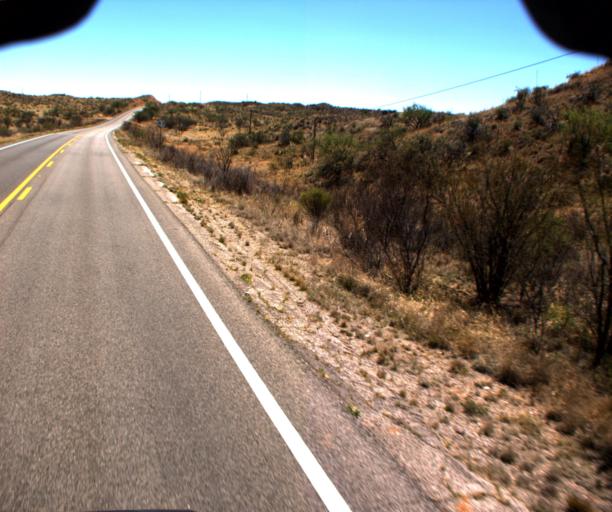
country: US
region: Arizona
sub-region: Pima County
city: Corona de Tucson
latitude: 31.7317
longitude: -110.6598
